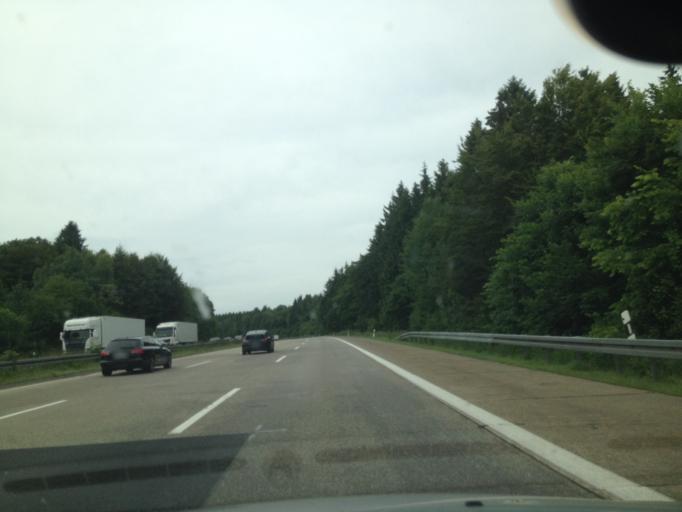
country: DE
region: North Rhine-Westphalia
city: Meinerzhagen
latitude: 51.0860
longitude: 7.6894
